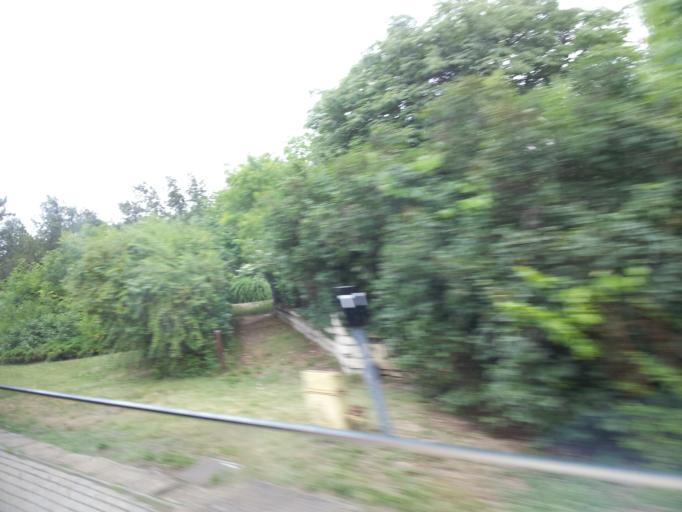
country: HU
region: Somogy
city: Balatonszarszo
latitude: 46.9050
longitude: 17.8085
